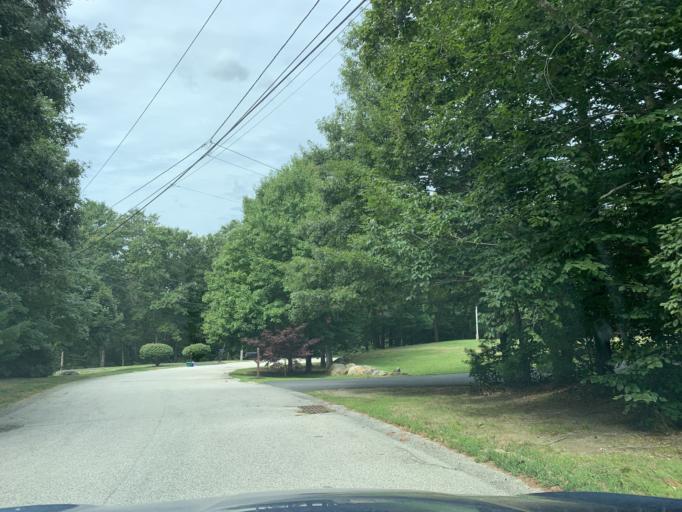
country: US
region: Rhode Island
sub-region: Washington County
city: Exeter
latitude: 41.5356
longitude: -71.6174
